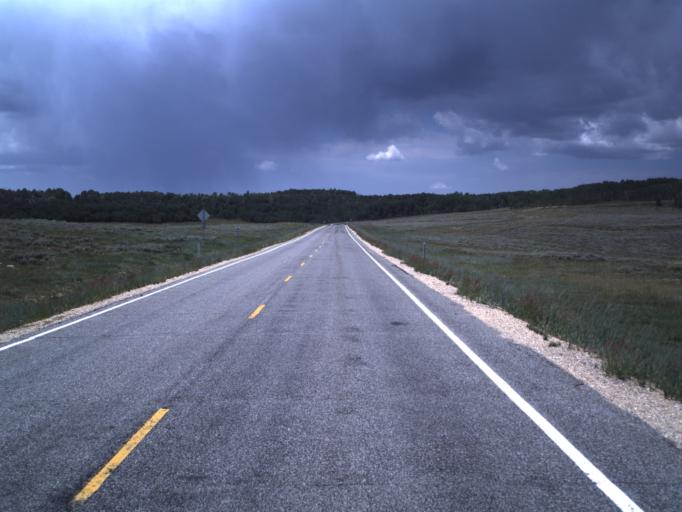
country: US
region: Utah
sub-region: Sanpete County
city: Fairview
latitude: 39.6691
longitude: -111.3064
